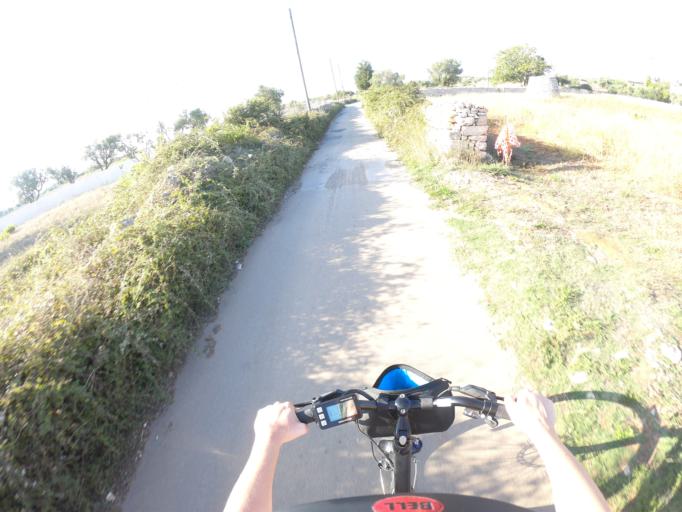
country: IT
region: Apulia
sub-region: Provincia di Lecce
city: Castrignano del Capo
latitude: 39.8396
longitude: 18.3555
